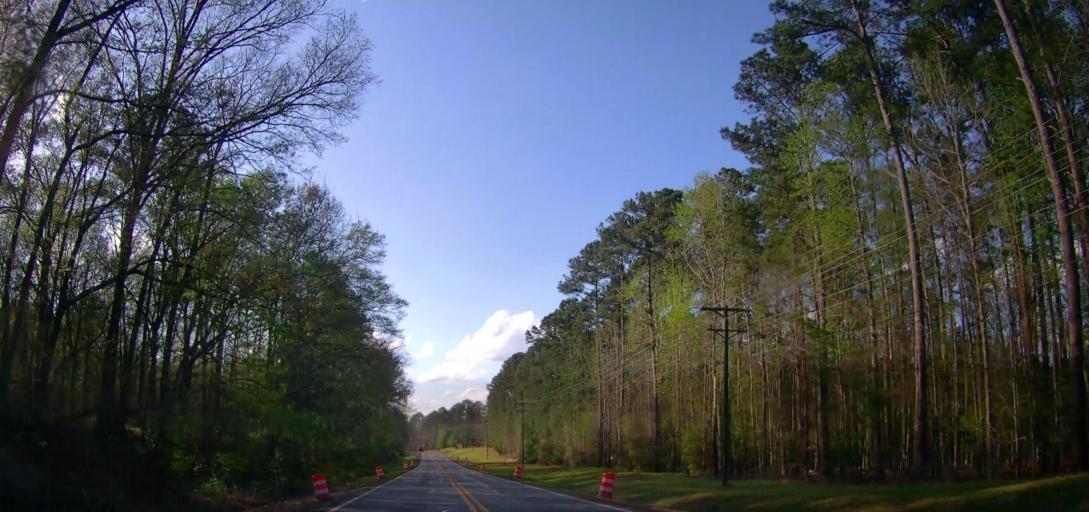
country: US
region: Georgia
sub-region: Baldwin County
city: Milledgeville
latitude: 33.1568
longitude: -83.3508
